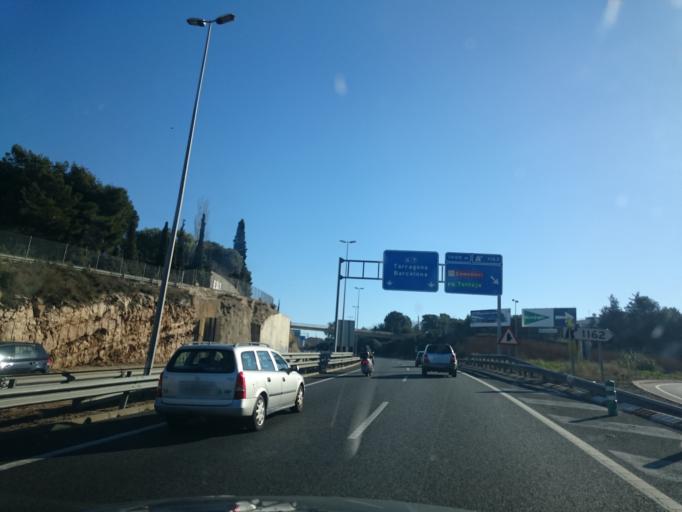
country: ES
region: Catalonia
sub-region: Provincia de Tarragona
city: Tarragona
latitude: 41.1252
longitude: 1.2450
